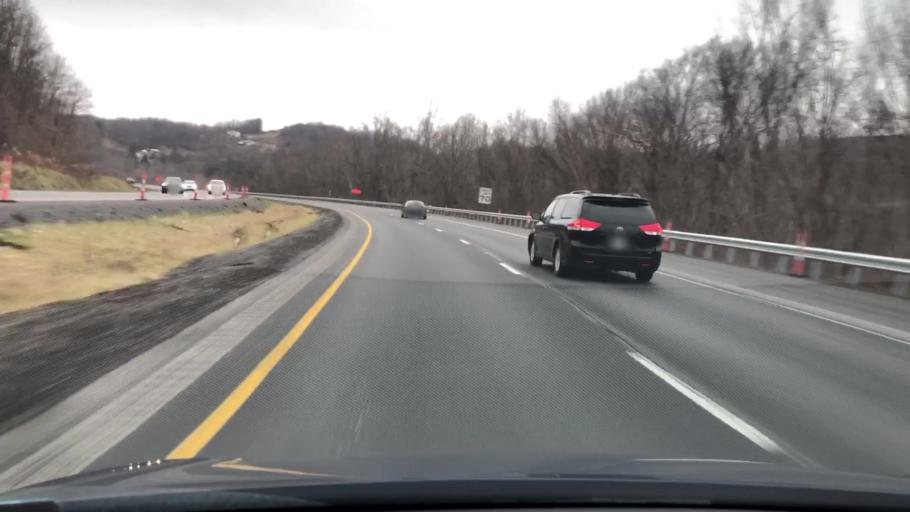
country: US
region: West Virginia
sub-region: Monongalia County
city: Star City
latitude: 39.6631
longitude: -80.0122
